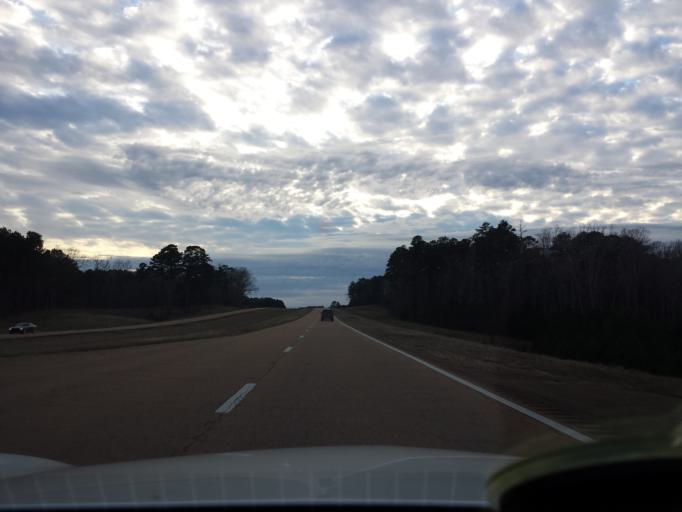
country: US
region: Mississippi
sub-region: Winston County
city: Louisville
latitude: 33.1909
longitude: -89.0012
